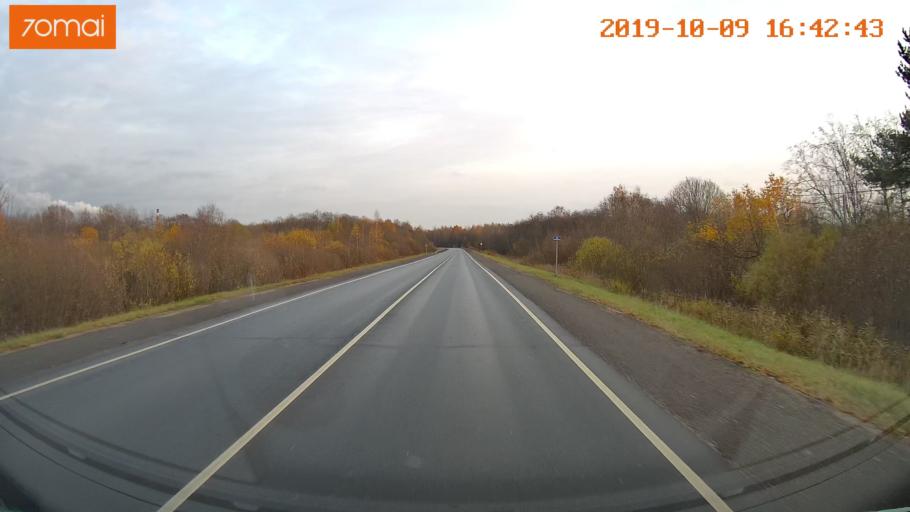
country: RU
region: Kostroma
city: Volgorechensk
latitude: 57.4592
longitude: 41.1060
